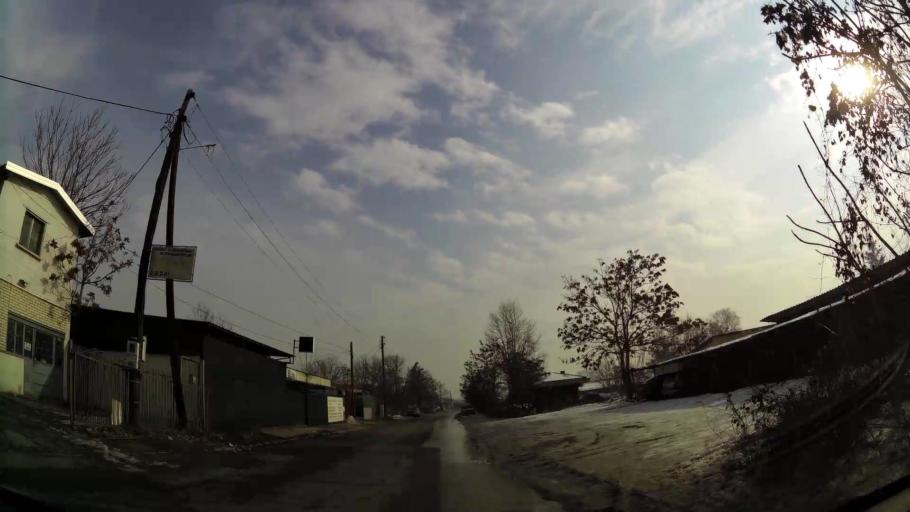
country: MK
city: Krushopek
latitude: 42.0133
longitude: 21.3759
